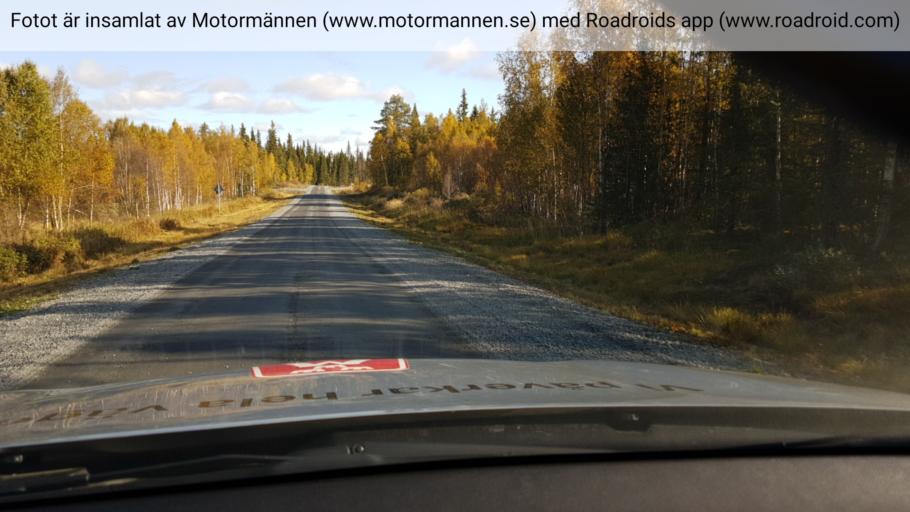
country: SE
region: Vaesterbotten
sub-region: Vilhelmina Kommun
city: Sjoberg
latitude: 64.7982
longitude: 15.9942
